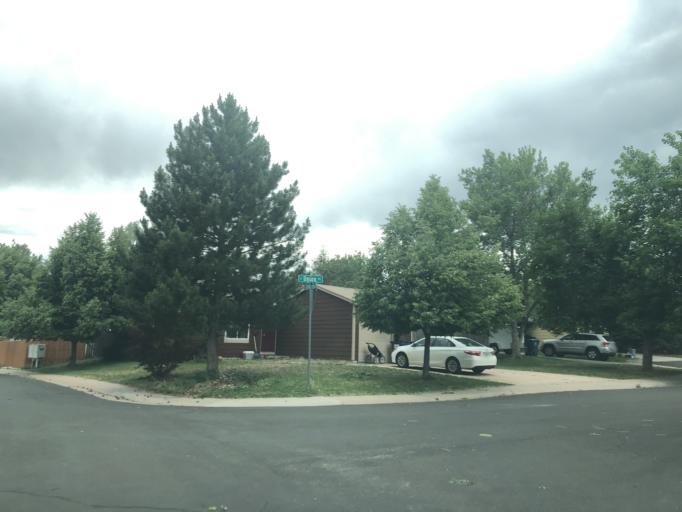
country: US
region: Colorado
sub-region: Arapahoe County
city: Dove Valley
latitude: 39.6305
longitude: -104.7840
